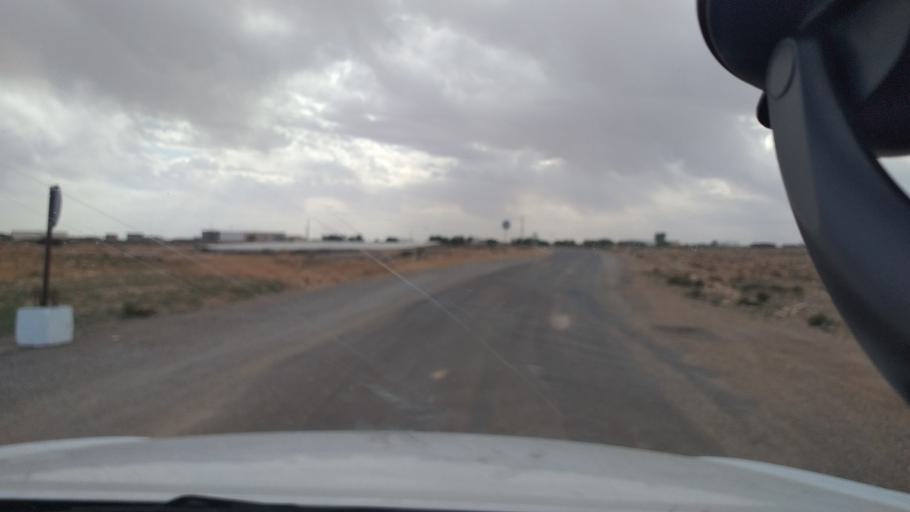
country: TN
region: Madanin
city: Medenine
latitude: 33.2971
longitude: 10.6089
